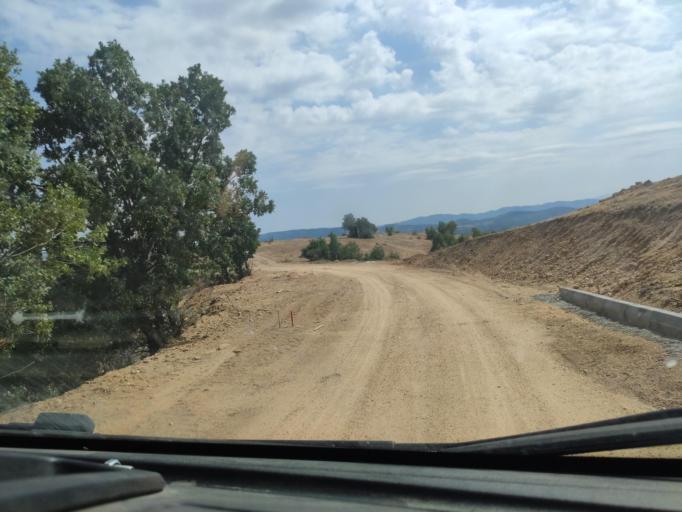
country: MK
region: Radovis
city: Radovish
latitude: 41.6692
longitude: 22.4049
